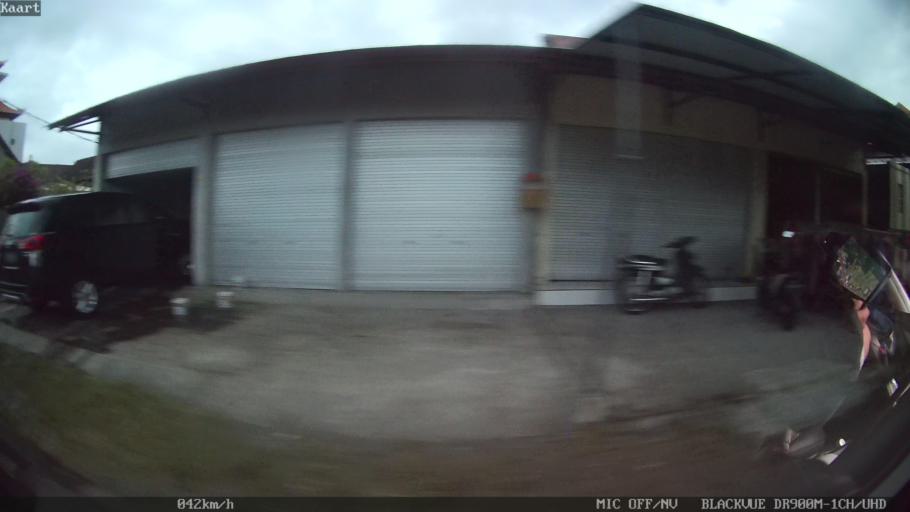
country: ID
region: Bali
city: Banjar Pasekan
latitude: -8.6283
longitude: 115.2920
